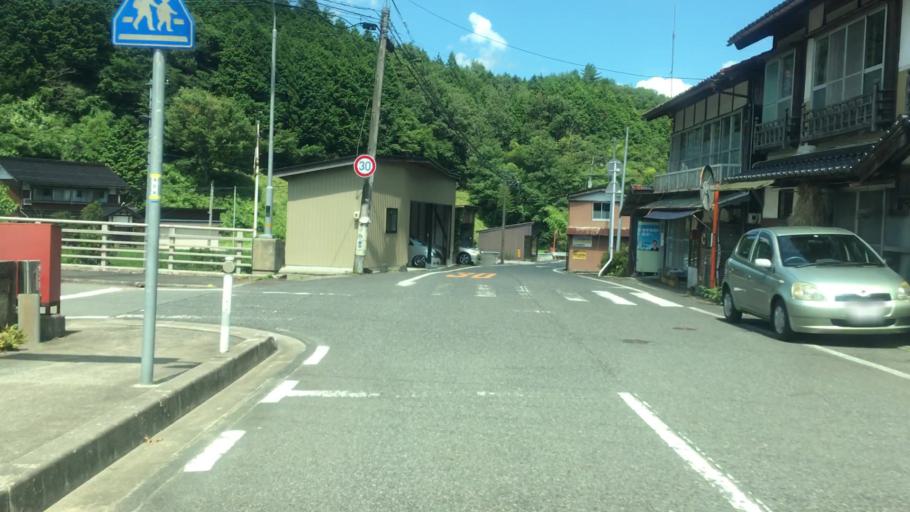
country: JP
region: Okayama
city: Tsuyama
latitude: 35.2128
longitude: 134.2106
